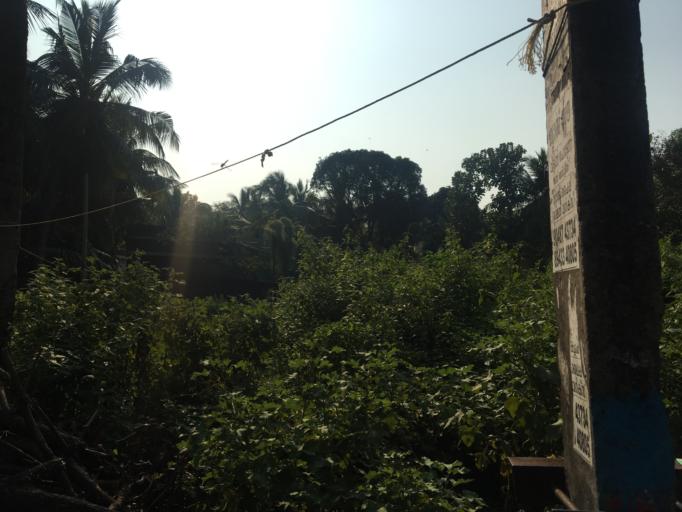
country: IN
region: Kerala
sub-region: Ernakulam
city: Cochin
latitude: 9.9502
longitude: 76.3076
